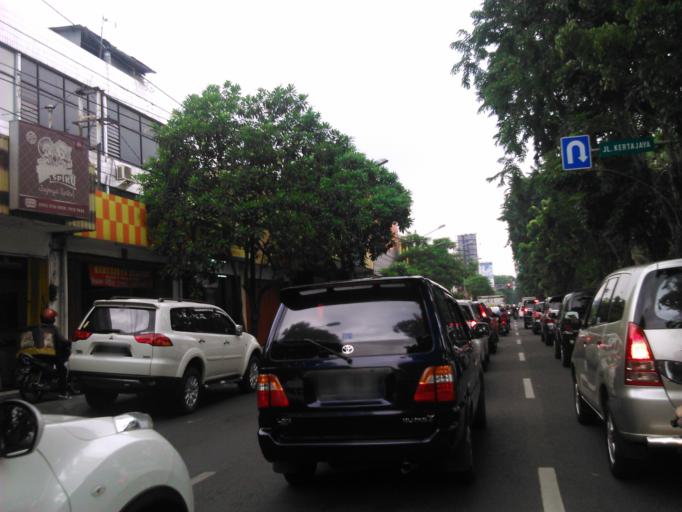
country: ID
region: East Java
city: Gubengairlangga
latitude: -7.2788
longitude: 112.7578
